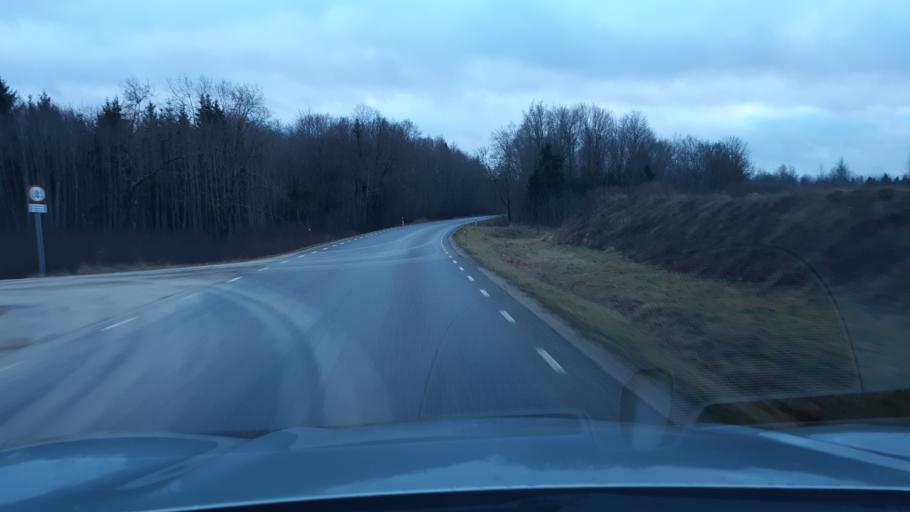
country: EE
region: Raplamaa
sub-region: Kohila vald
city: Kohila
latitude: 59.1120
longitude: 24.6833
